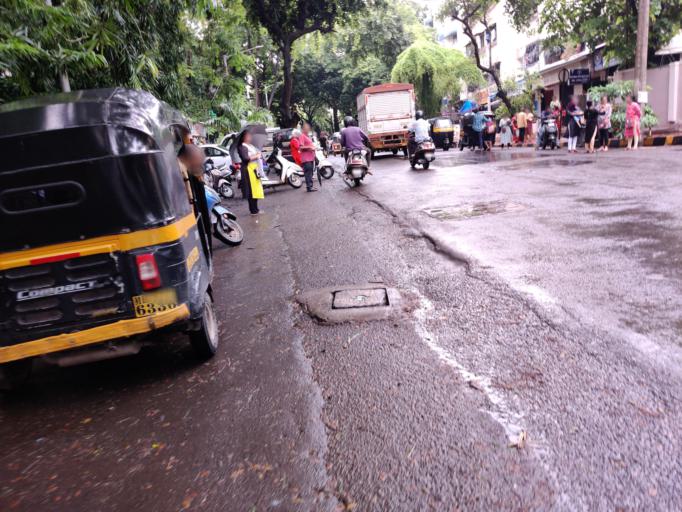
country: IN
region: Maharashtra
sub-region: Mumbai Suburban
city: Borivli
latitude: 19.2480
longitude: 72.8530
